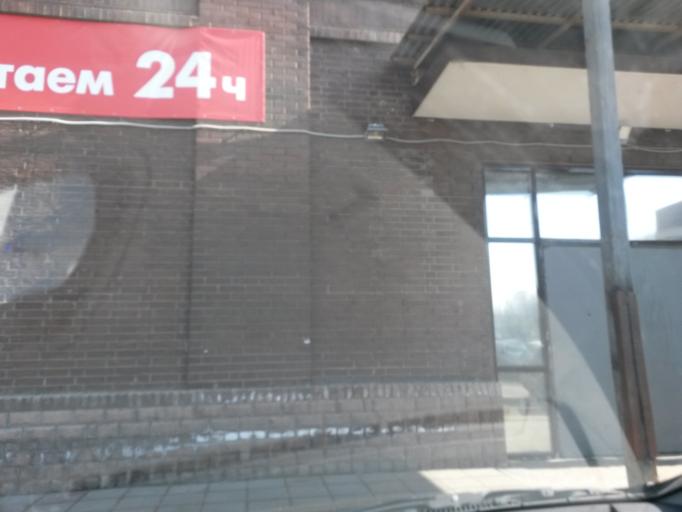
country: RU
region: Moscow
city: Annino
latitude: 55.5445
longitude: 37.5876
